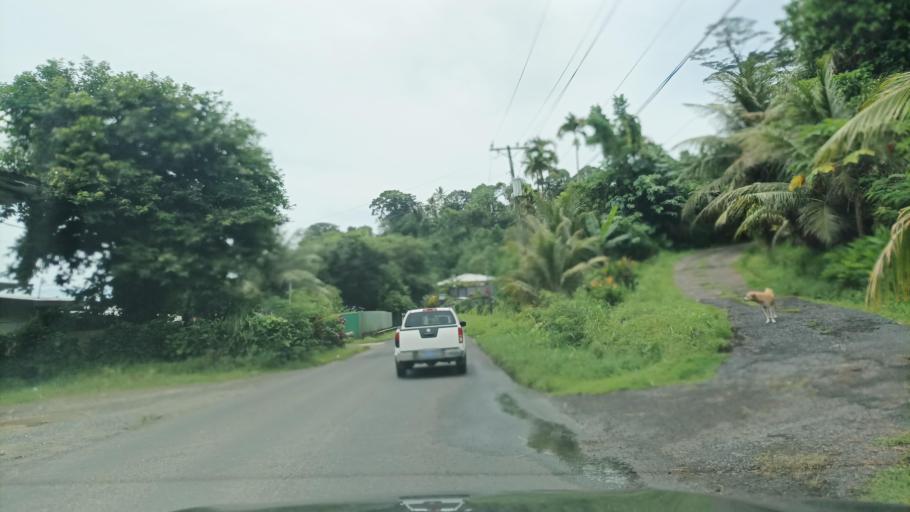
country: FM
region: Pohnpei
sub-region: Kolonia Municipality
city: Kolonia Town
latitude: 6.9566
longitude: 158.1996
